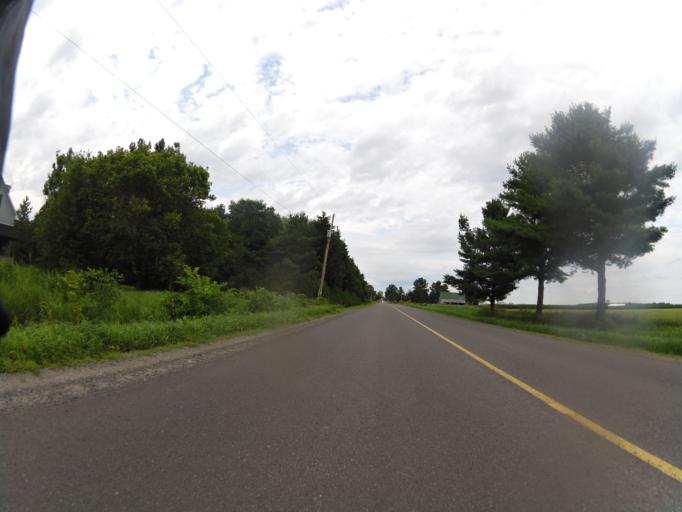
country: CA
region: Ontario
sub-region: Lanark County
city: Smiths Falls
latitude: 44.9985
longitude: -75.7570
